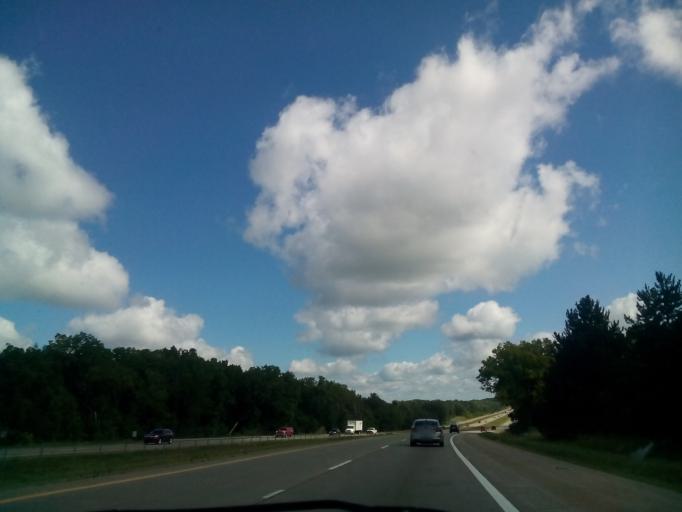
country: US
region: Michigan
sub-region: Genesee County
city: Linden
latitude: 42.7508
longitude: -83.7636
